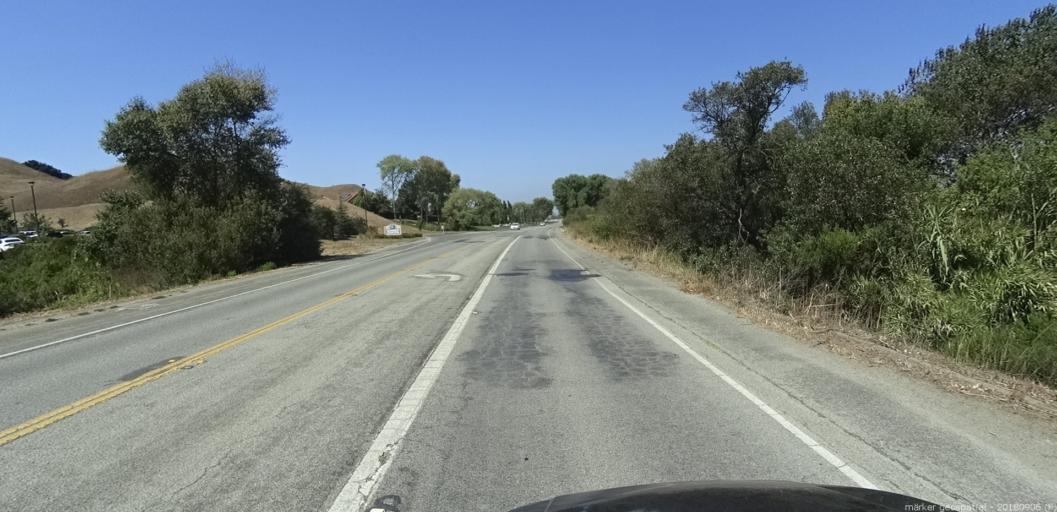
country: US
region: California
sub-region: Monterey County
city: Salinas
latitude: 36.6165
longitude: -121.6590
